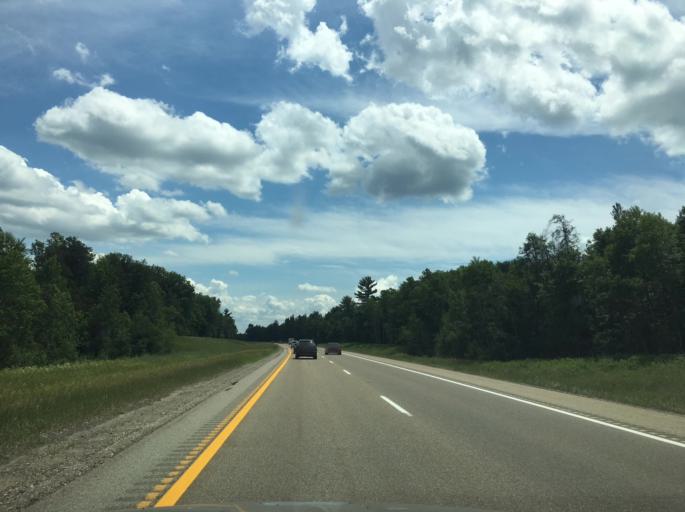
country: US
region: Michigan
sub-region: Crawford County
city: Grayling
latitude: 44.5512
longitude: -84.7042
